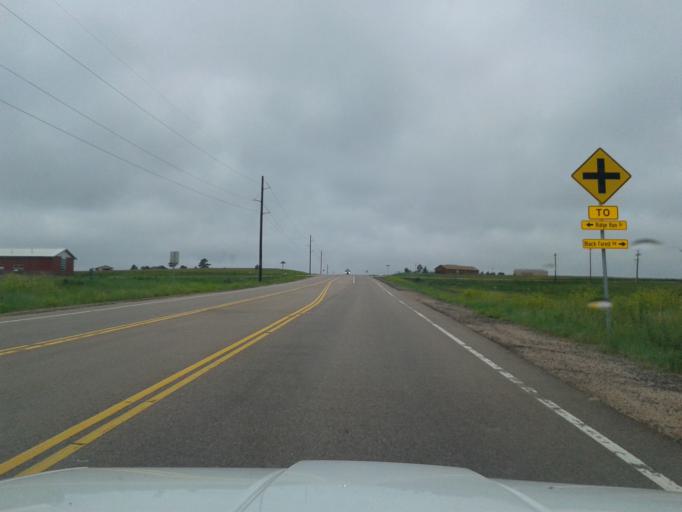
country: US
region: Colorado
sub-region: El Paso County
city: Black Forest
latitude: 39.0712
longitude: -104.6933
